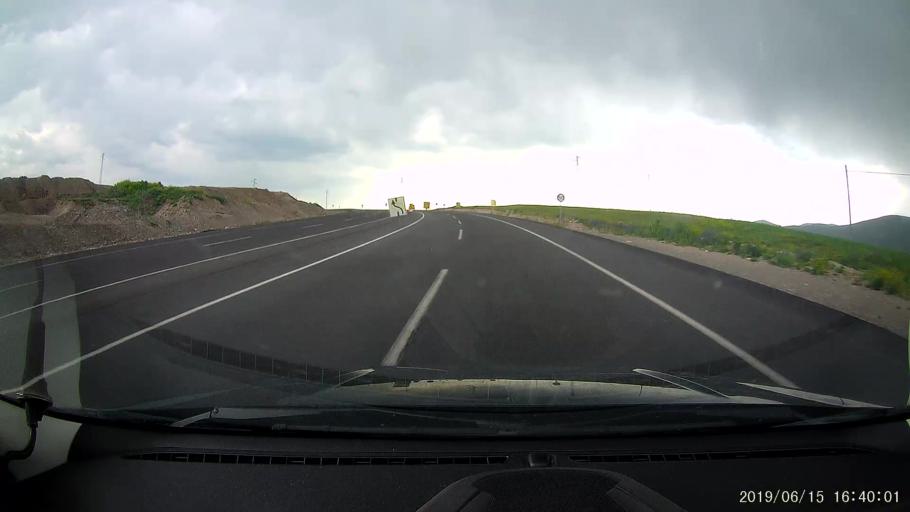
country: TR
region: Ardahan
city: Haskoy
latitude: 40.9748
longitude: 42.8934
